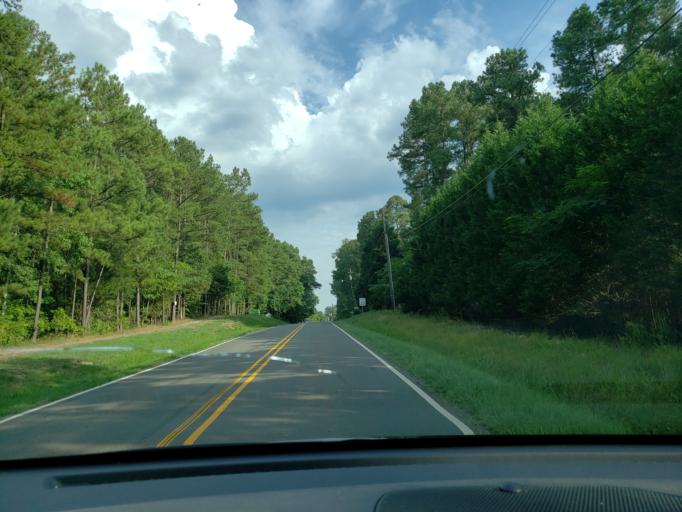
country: US
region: North Carolina
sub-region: Orange County
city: Chapel Hill
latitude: 35.9030
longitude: -78.9820
